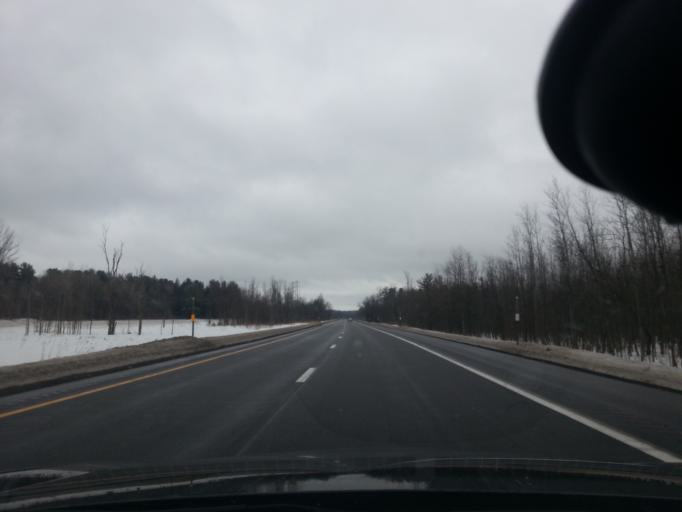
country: US
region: New York
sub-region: Oswego County
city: Central Square
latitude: 43.3444
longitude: -76.1233
